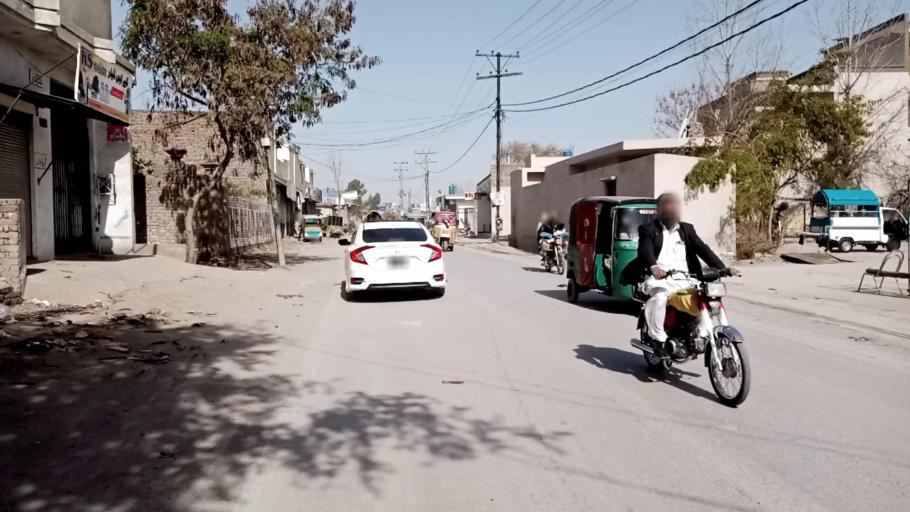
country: PK
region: Khyber Pakhtunkhwa
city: Peshawar
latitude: 34.0137
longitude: 71.6470
